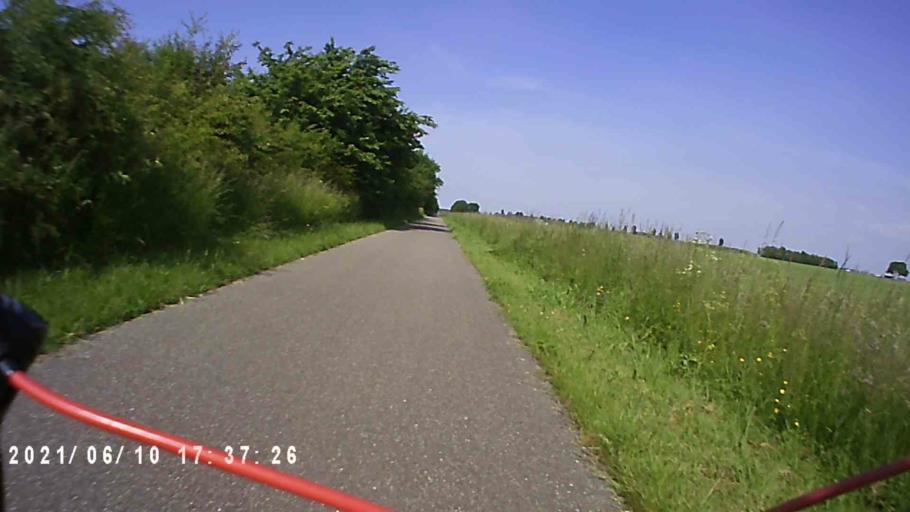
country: NL
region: Groningen
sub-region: Gemeente Zuidhorn
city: Grijpskerk
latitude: 53.3217
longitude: 6.2751
